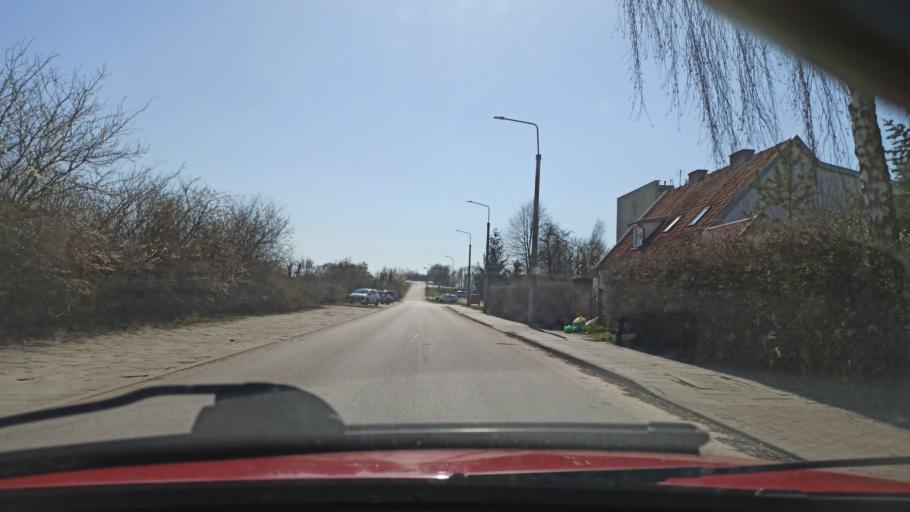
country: PL
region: Warmian-Masurian Voivodeship
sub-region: Powiat elblaski
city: Elblag
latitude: 54.1425
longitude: 19.4085
